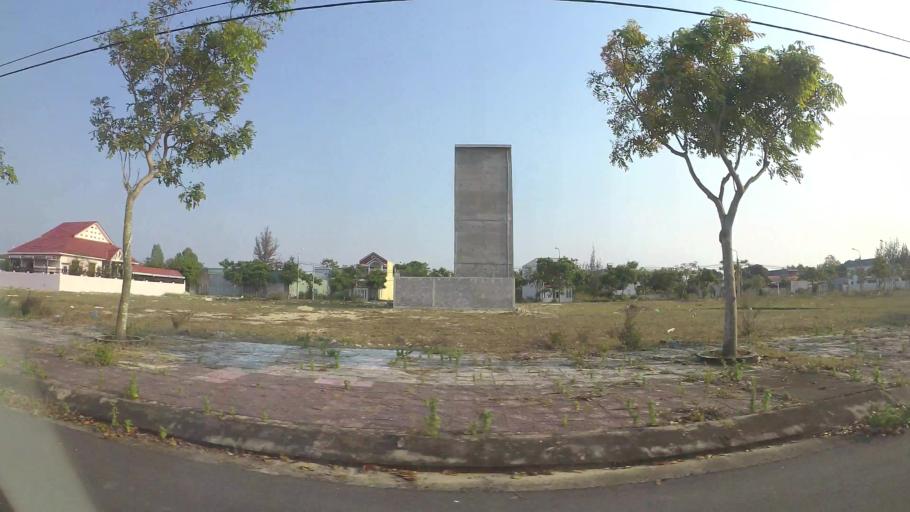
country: VN
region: Da Nang
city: Ngu Hanh Son
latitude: 15.9595
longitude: 108.2606
